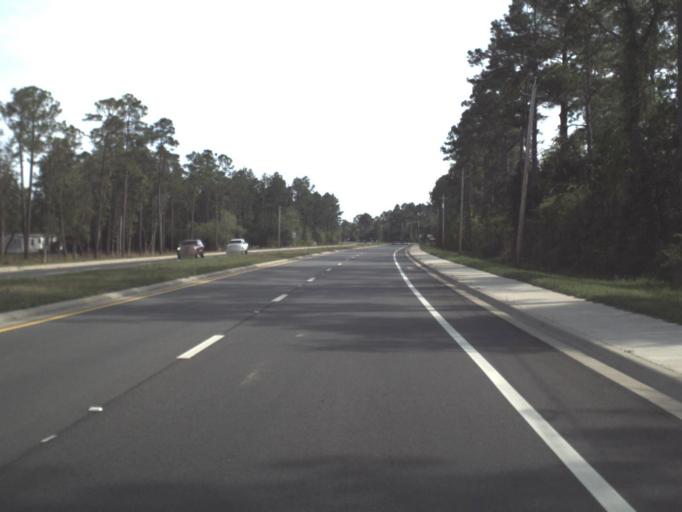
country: US
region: Florida
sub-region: Santa Rosa County
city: Holley
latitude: 30.4621
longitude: -86.9100
